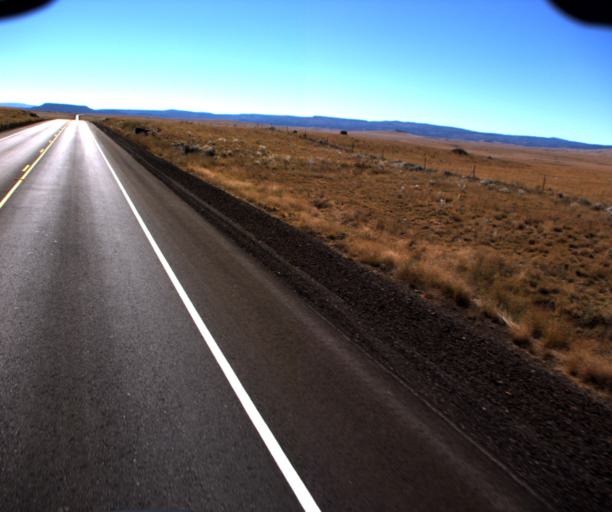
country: US
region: Arizona
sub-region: Apache County
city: Springerville
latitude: 34.2262
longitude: -109.3386
